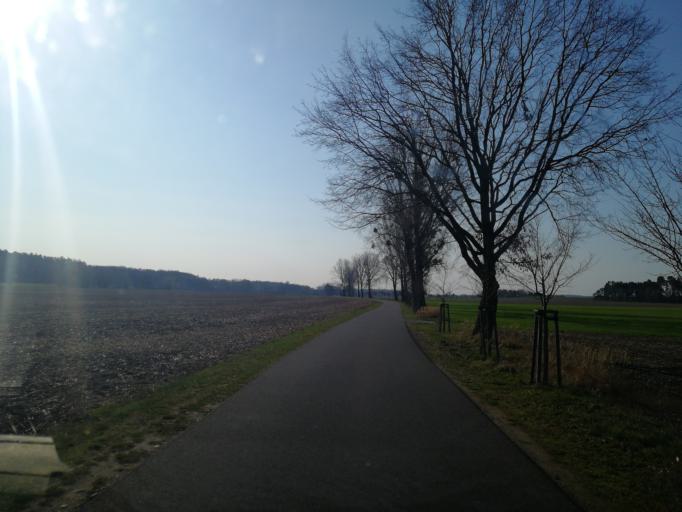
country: DE
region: Brandenburg
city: Drahnsdorf
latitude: 51.8888
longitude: 13.5803
